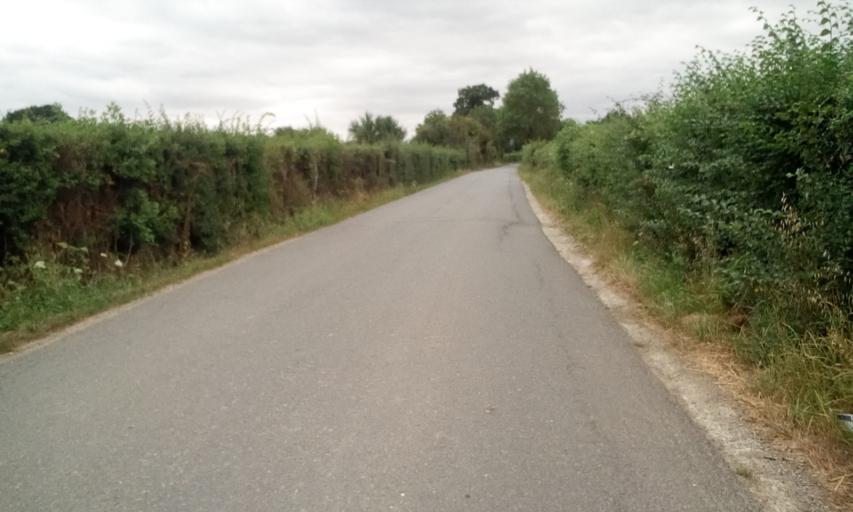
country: FR
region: Lower Normandy
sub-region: Departement du Calvados
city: Troarn
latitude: 49.1926
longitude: -0.1822
